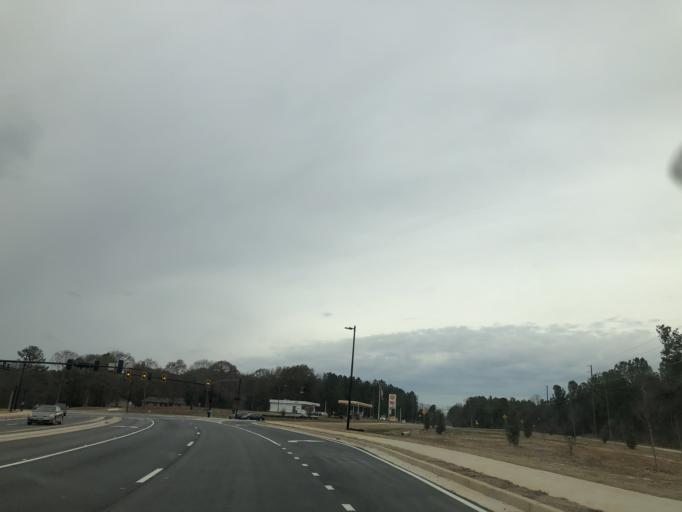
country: US
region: Georgia
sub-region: Clayton County
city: Conley
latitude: 33.6247
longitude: -84.2554
